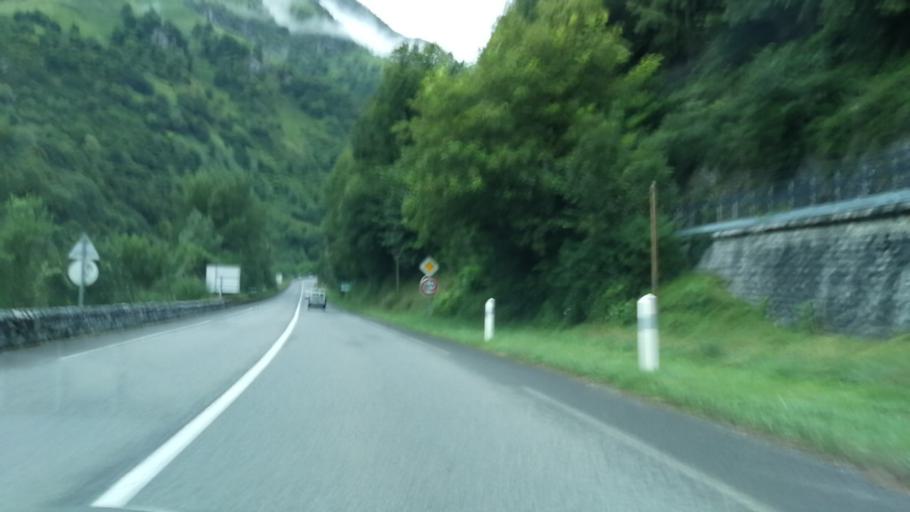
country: FR
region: Aquitaine
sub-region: Departement des Pyrenees-Atlantiques
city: Arette
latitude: 43.0119
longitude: -0.6030
